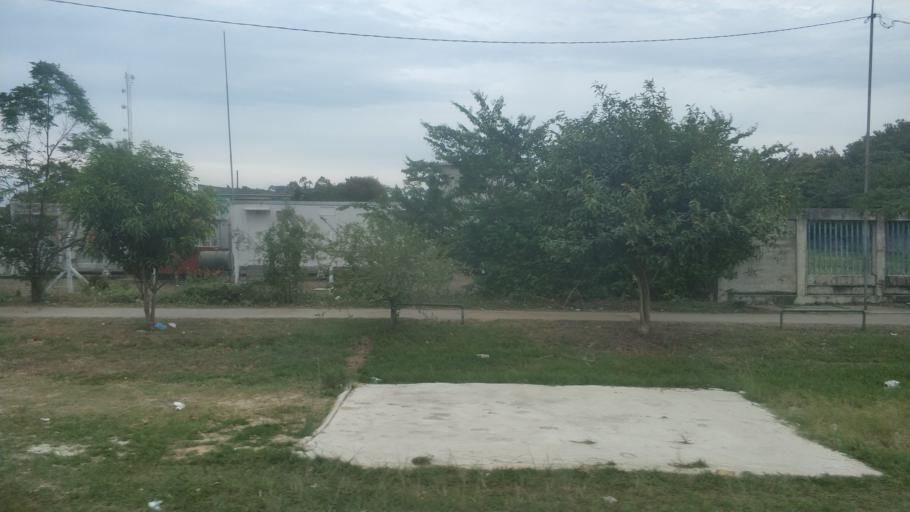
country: BR
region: Rio de Janeiro
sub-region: Seropedica
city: Seropedica
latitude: -22.7908
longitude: -43.6516
